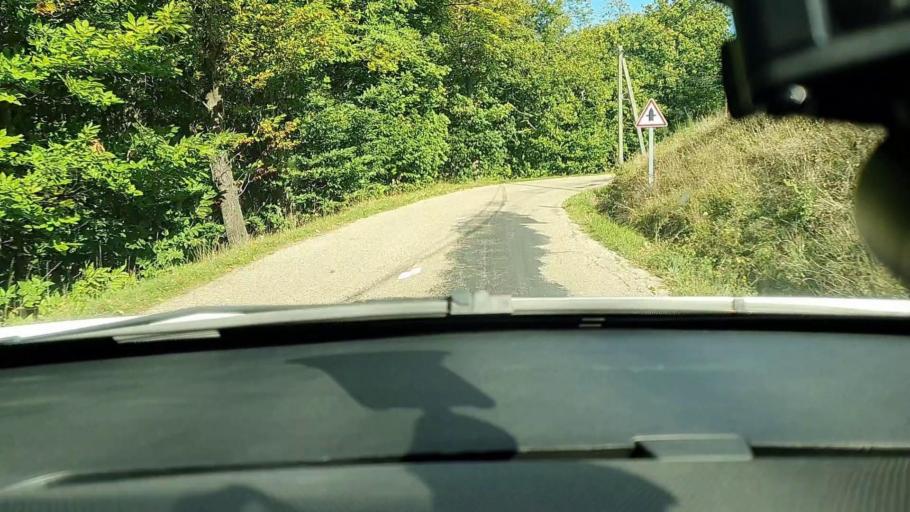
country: FR
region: Rhone-Alpes
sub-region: Departement de l'Ardeche
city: Les Vans
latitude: 44.4176
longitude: 4.0212
